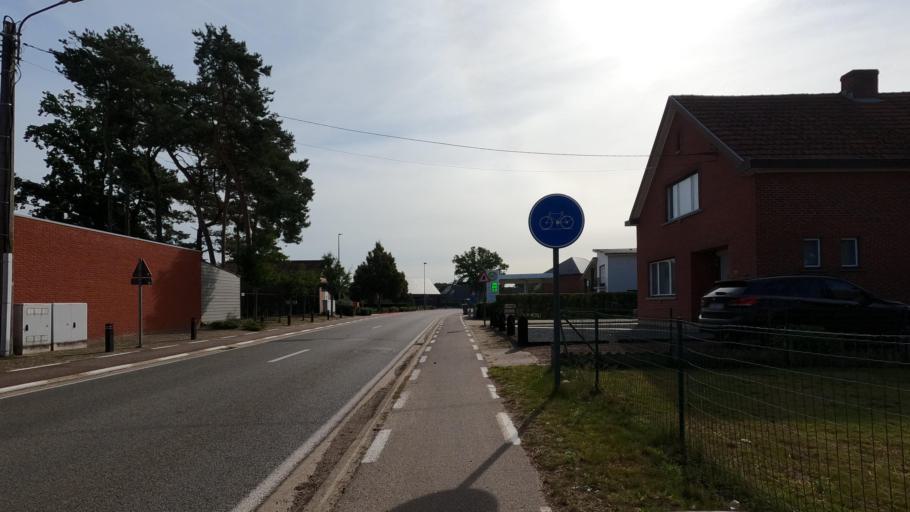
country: BE
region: Flanders
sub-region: Provincie Antwerpen
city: Herselt
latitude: 51.0309
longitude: 4.8950
